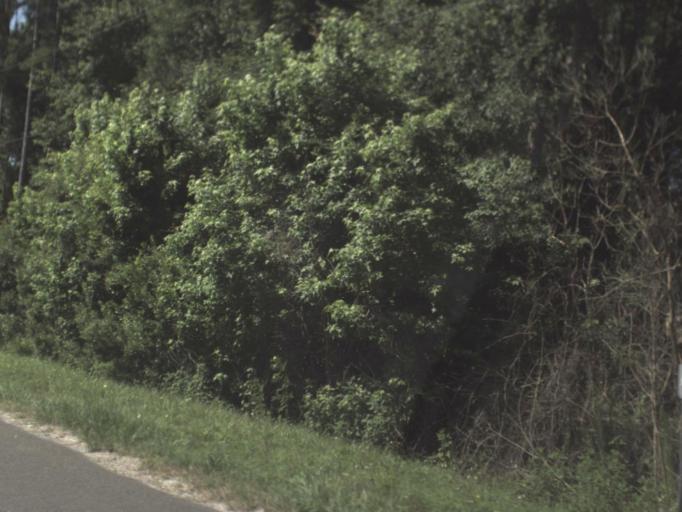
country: US
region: Florida
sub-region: Nassau County
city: Nassau Village-Ratliff
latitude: 30.5208
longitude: -81.7680
